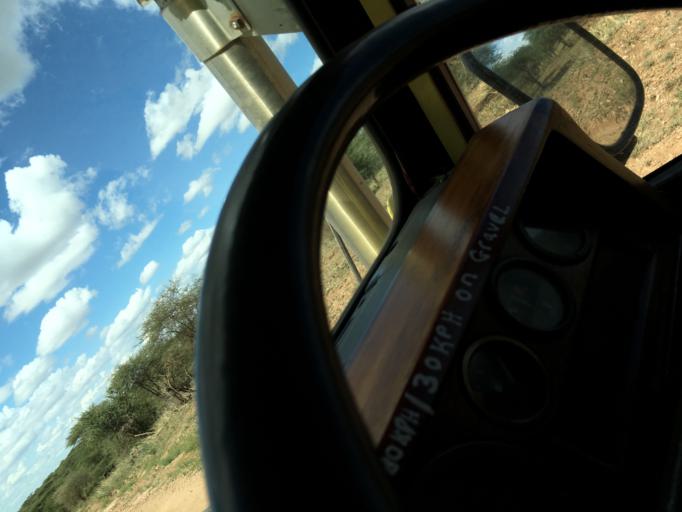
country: TZ
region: Mara
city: Mugumu
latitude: -2.3190
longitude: 34.8460
